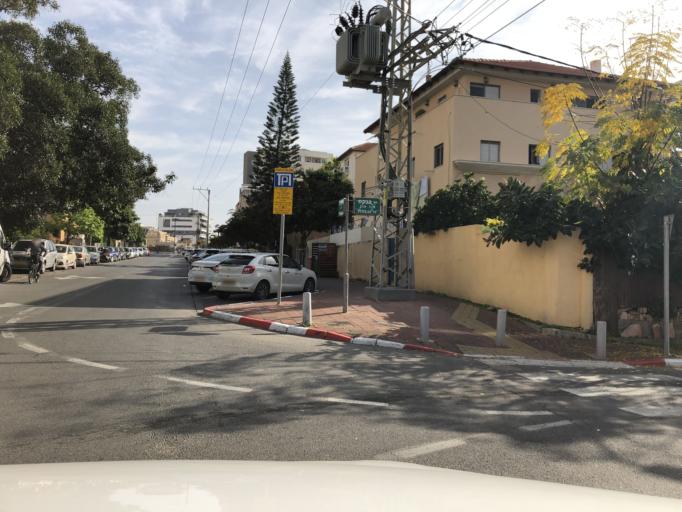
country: IL
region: Tel Aviv
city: Bene Beraq
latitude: 32.0700
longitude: 34.8307
